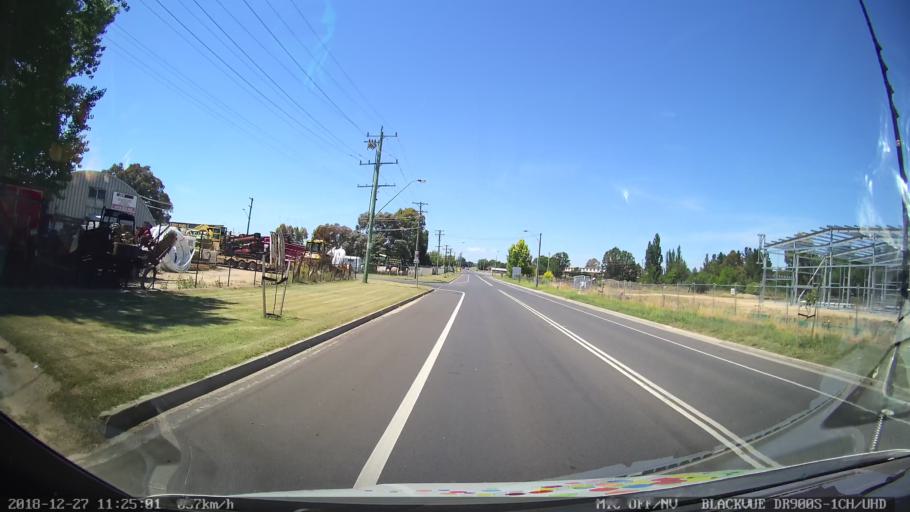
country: AU
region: New South Wales
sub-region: Bathurst Regional
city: Bathurst
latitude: -33.4382
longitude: 149.5785
